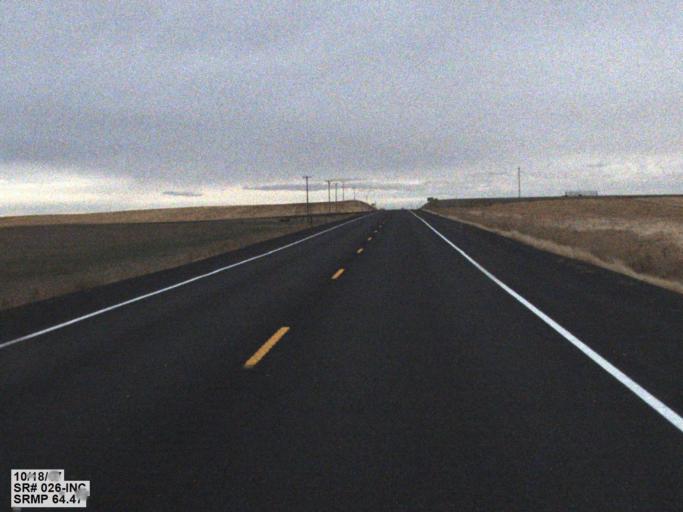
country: US
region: Washington
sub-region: Franklin County
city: Connell
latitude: 46.7944
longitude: -118.6764
